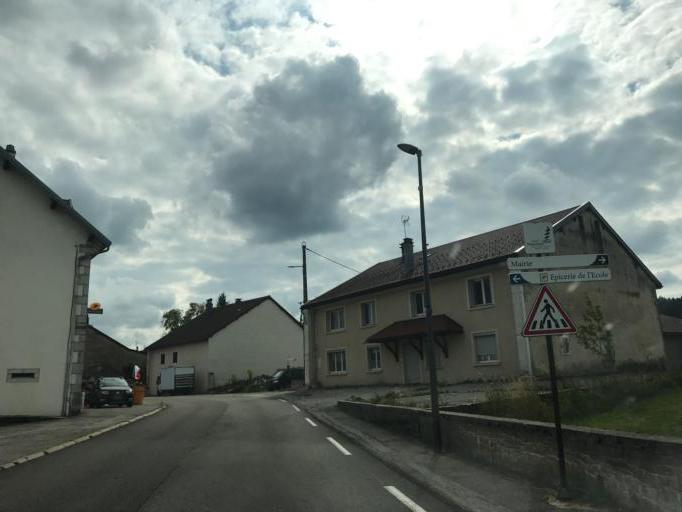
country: FR
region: Franche-Comte
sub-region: Departement du Jura
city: Valfin-les-Saint-Claude
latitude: 46.5093
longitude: 5.8686
